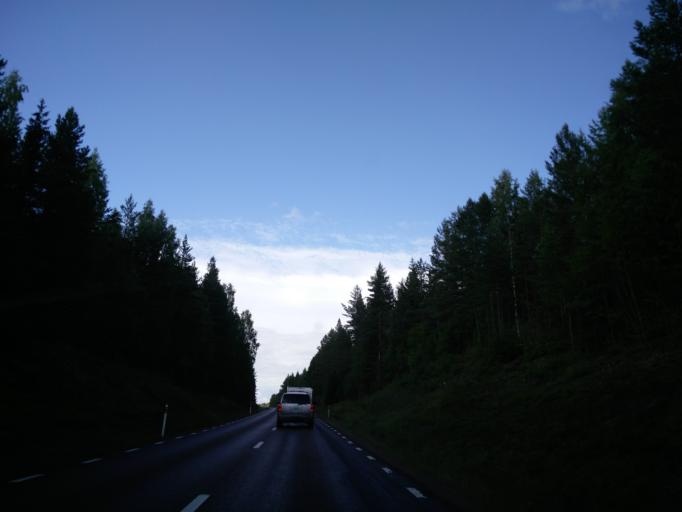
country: SE
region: Vaermland
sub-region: Hagfors Kommun
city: Ekshaerad
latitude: 60.4581
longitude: 13.2955
